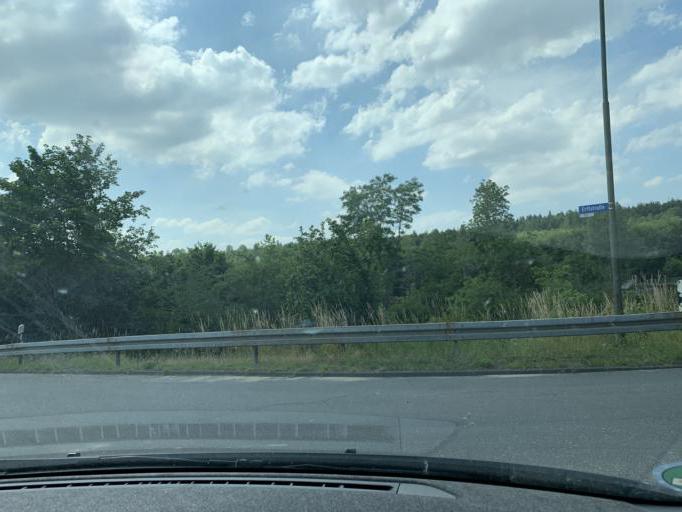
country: DE
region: North Rhine-Westphalia
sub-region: Regierungsbezirk Dusseldorf
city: Grevenbroich
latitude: 51.0480
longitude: 6.5650
